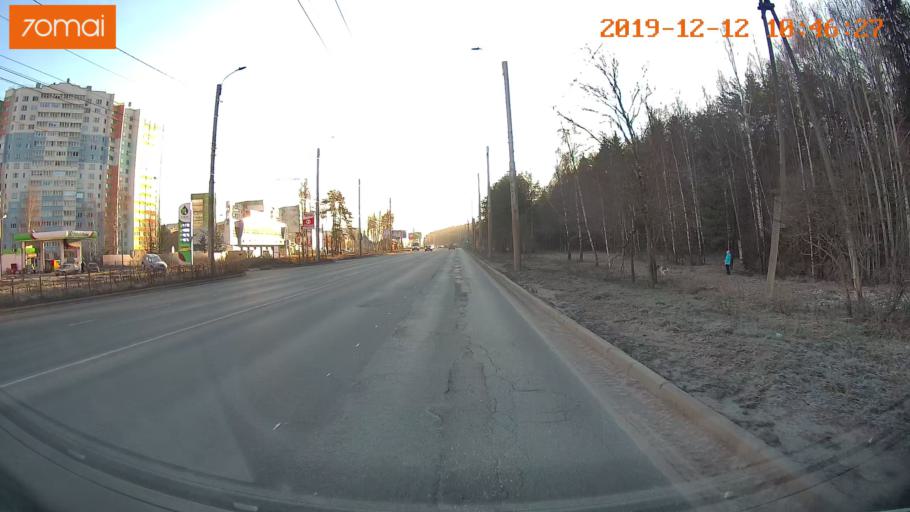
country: RU
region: Ivanovo
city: Kokhma
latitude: 56.9534
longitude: 41.0437
